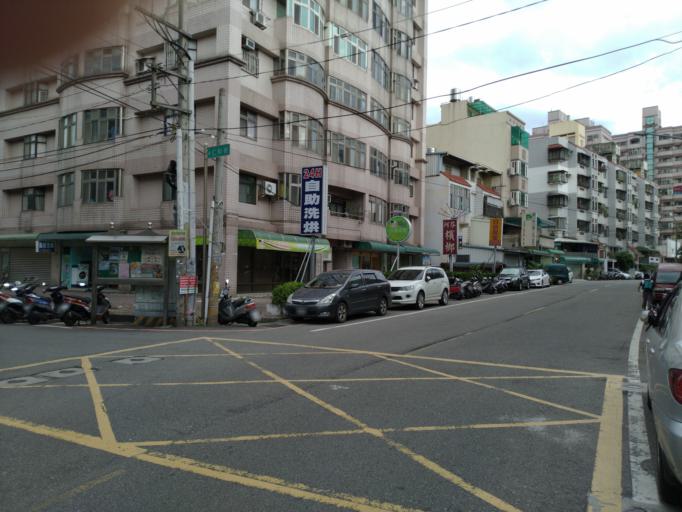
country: TW
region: Taiwan
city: Taoyuan City
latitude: 24.9799
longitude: 121.2574
